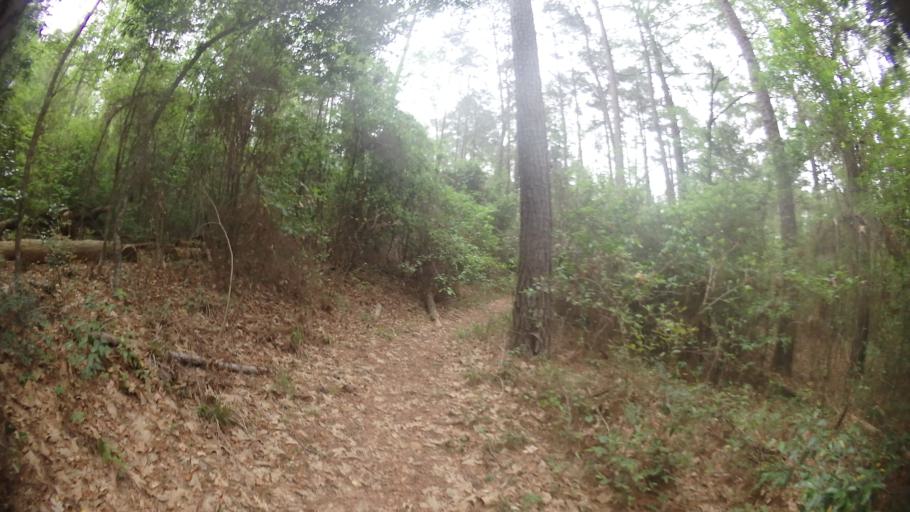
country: US
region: Texas
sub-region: Nacogdoches County
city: Nacogdoches
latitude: 31.6215
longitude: -94.6362
